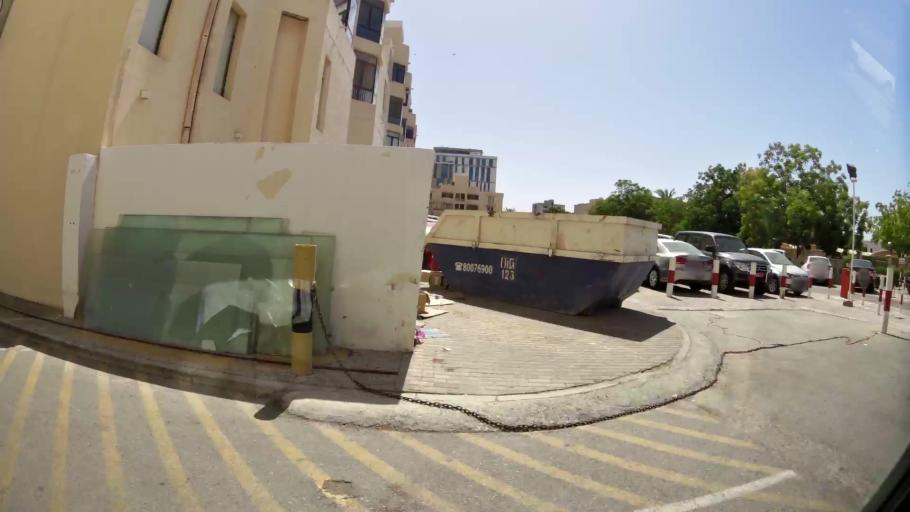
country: OM
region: Muhafazat Masqat
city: Bawshar
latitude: 23.5899
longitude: 58.3624
